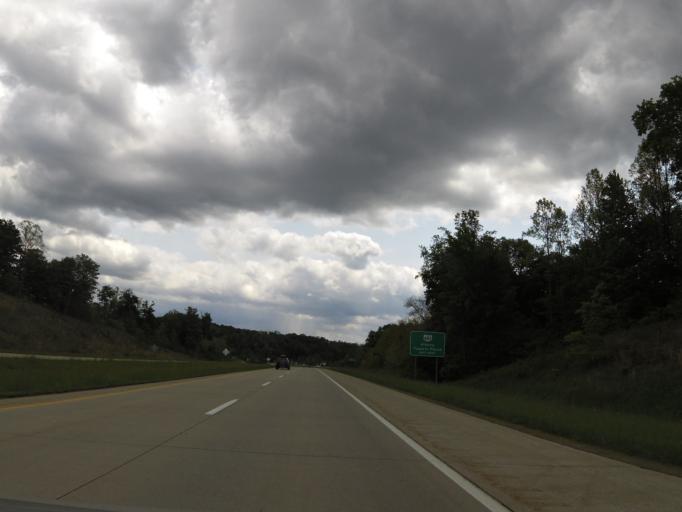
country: US
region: Ohio
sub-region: Meigs County
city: Pomeroy
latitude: 39.1487
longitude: -82.0278
